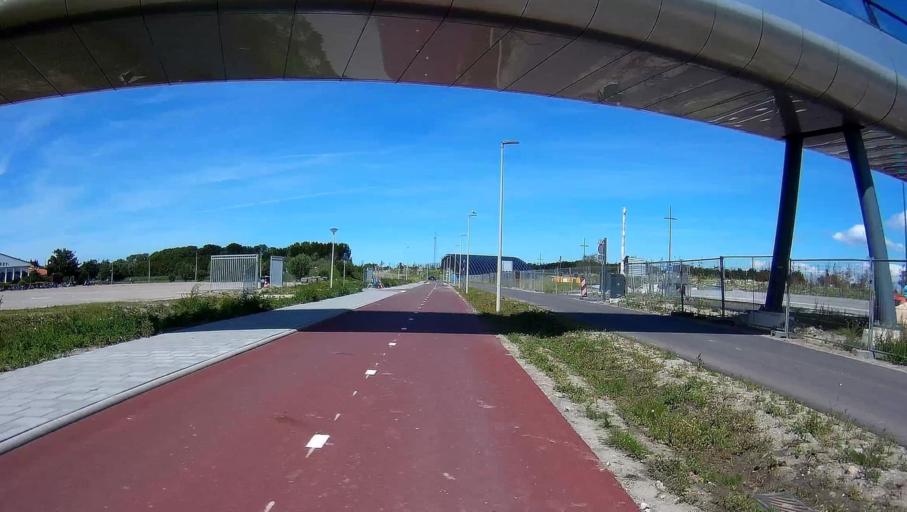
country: NL
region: South Holland
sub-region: Gemeente Den Haag
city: Ypenburg
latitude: 52.0513
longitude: 4.3537
